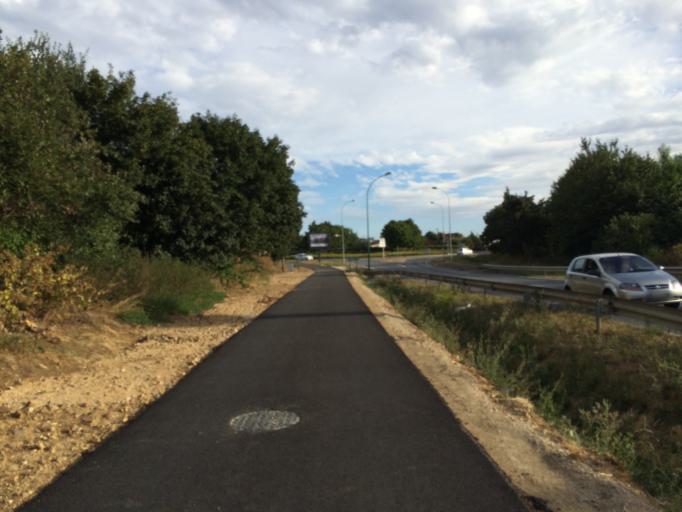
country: FR
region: Ile-de-France
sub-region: Departement de l'Essonne
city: Morangis
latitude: 48.7074
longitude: 2.3514
